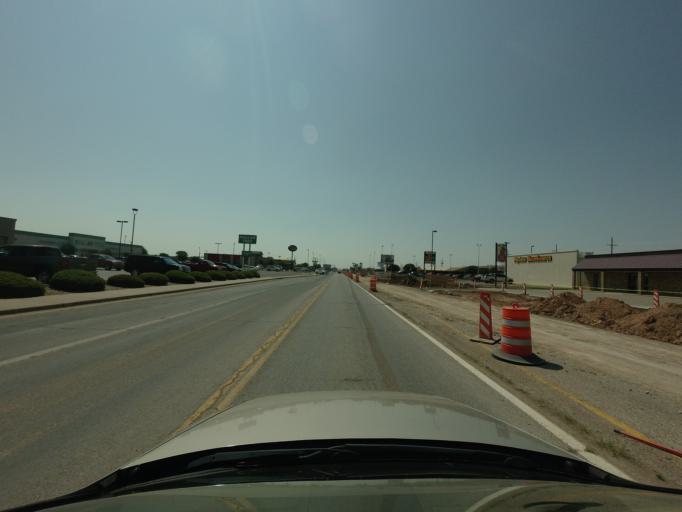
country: US
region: New Mexico
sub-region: Curry County
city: Clovis
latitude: 34.4380
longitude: -103.1964
